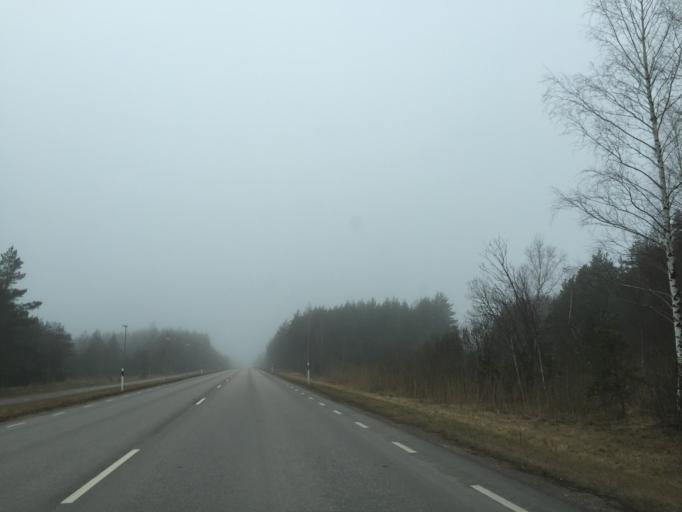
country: EE
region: Saare
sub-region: Kuressaare linn
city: Kuressaare
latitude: 58.2356
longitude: 22.4277
